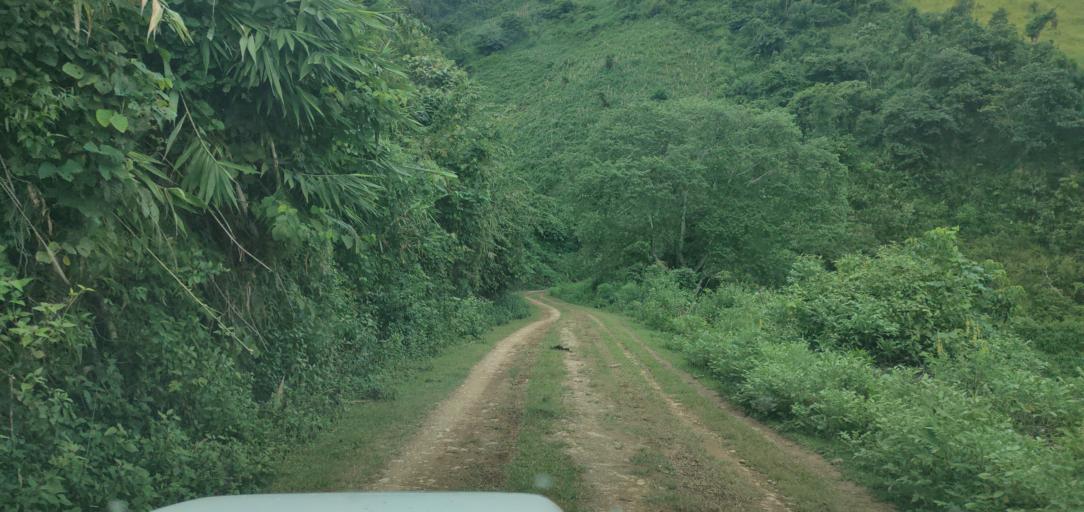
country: LA
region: Phongsali
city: Phongsali
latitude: 21.4407
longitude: 102.3190
